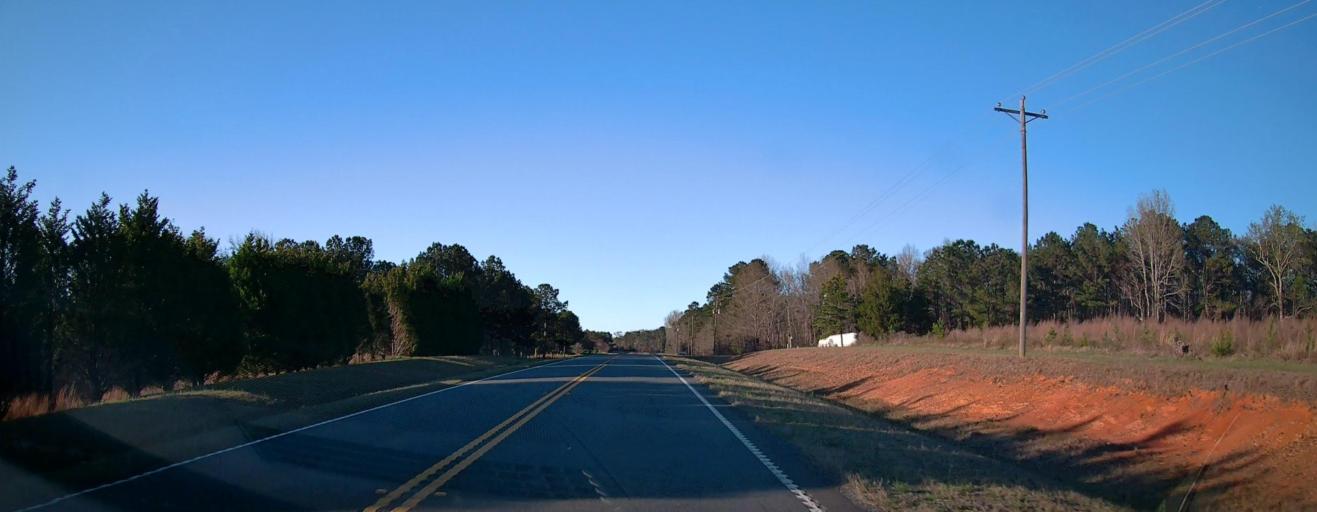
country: US
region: Georgia
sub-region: Talbot County
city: Talbotton
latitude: 32.6320
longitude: -84.5368
